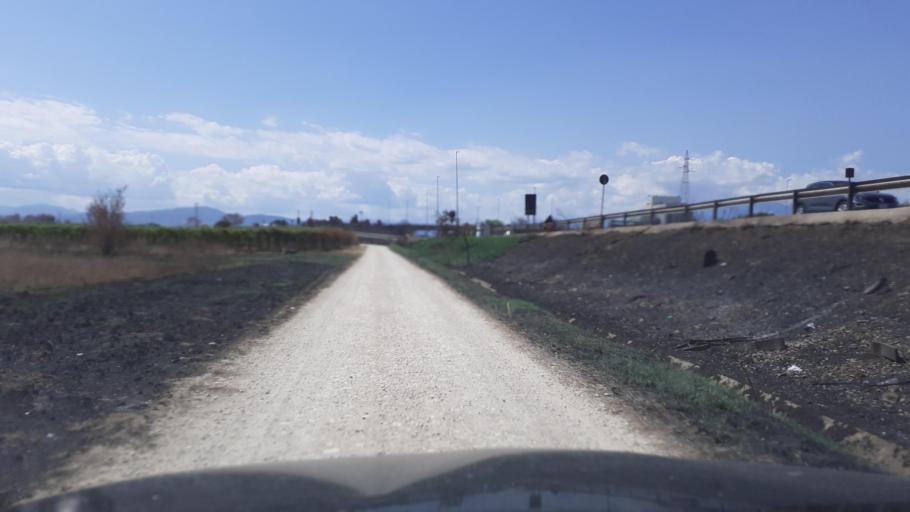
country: IT
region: Abruzzo
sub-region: Provincia di Chieti
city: Fossacesia
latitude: 42.2175
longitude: 14.4984
